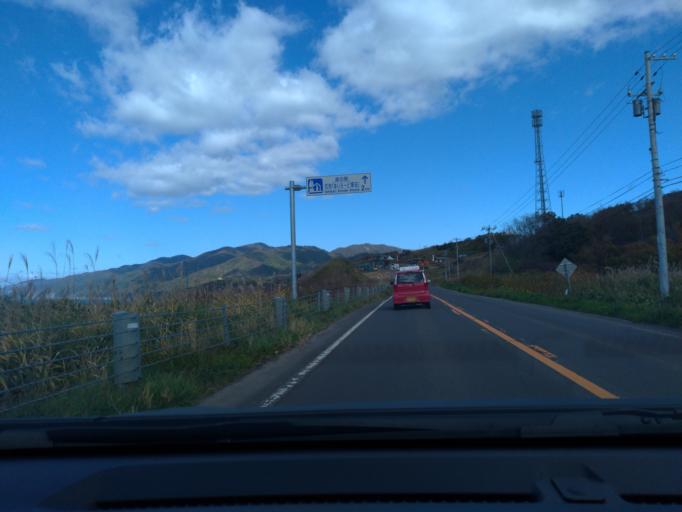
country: JP
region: Hokkaido
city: Ishikari
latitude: 43.3888
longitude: 141.4327
